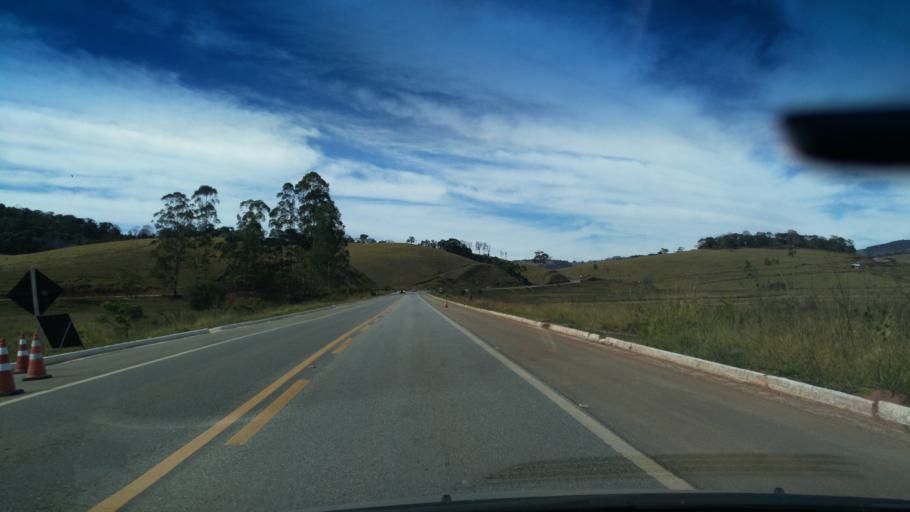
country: BR
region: Minas Gerais
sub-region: Borda Da Mata
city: Borda da Mata
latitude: -22.1506
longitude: -46.1280
